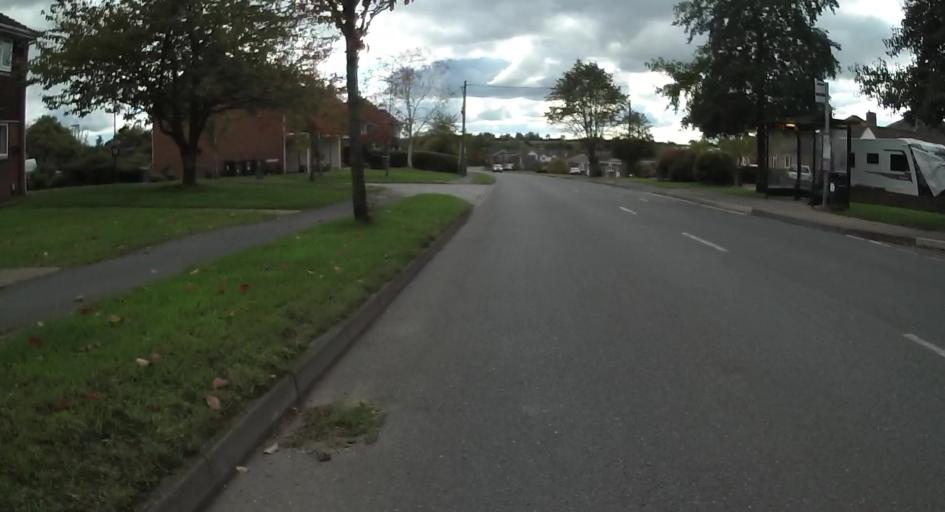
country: GB
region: England
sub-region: Surrey
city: Seale
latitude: 51.2382
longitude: -0.7303
